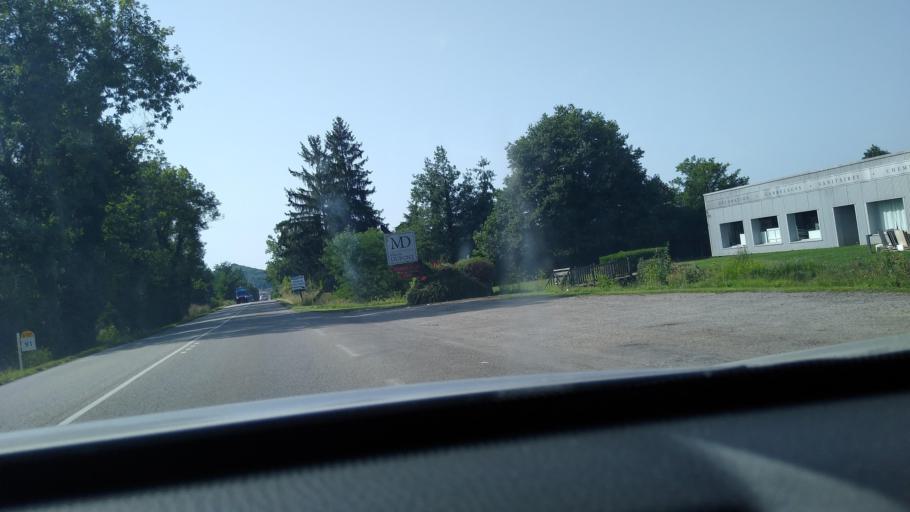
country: FR
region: Midi-Pyrenees
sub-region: Departement de l'Ariege
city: Saint-Lizier
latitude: 43.0223
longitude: 1.0967
